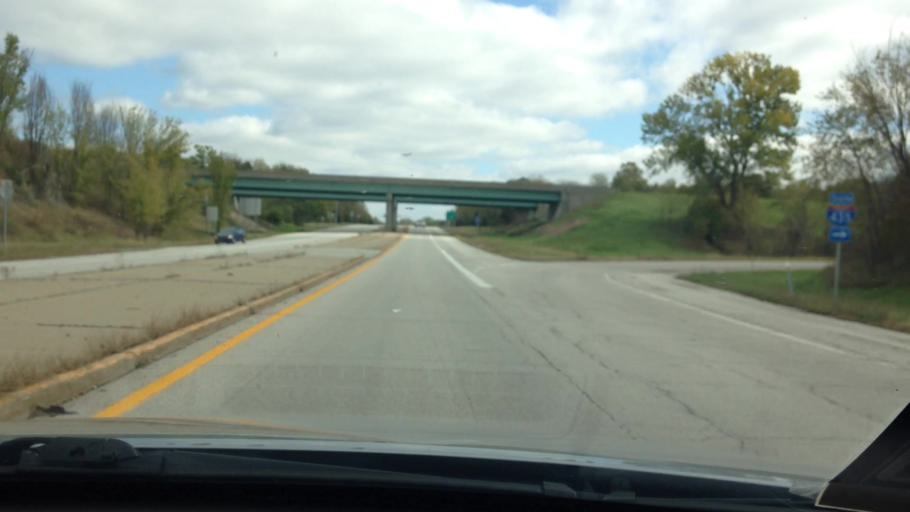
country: US
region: Missouri
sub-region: Platte County
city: Weatherby Lake
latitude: 39.2454
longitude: -94.7573
